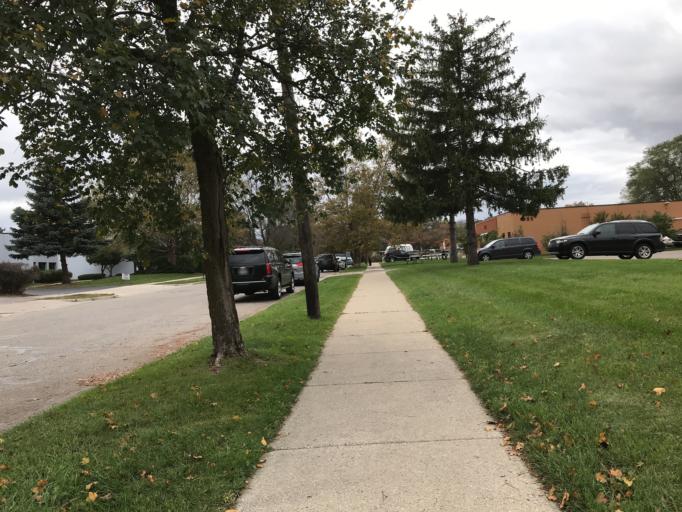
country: US
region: Michigan
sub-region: Washtenaw County
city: Ann Arbor
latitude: 42.2550
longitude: -83.7333
